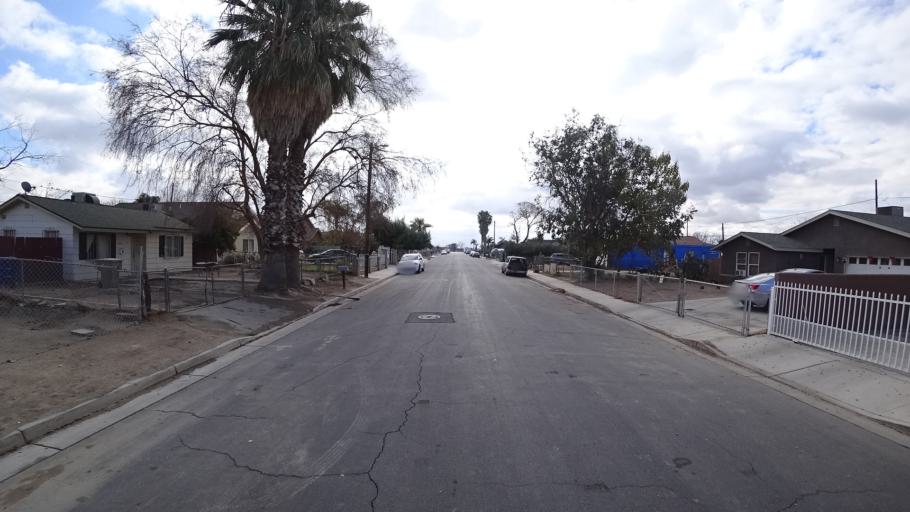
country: US
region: California
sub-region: Kern County
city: Greenfield
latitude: 35.3232
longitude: -118.9877
